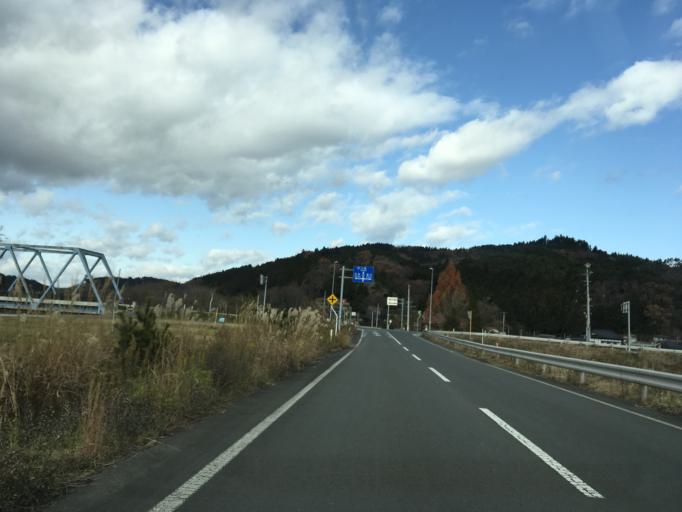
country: JP
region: Iwate
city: Ichinoseki
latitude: 38.8429
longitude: 141.2645
